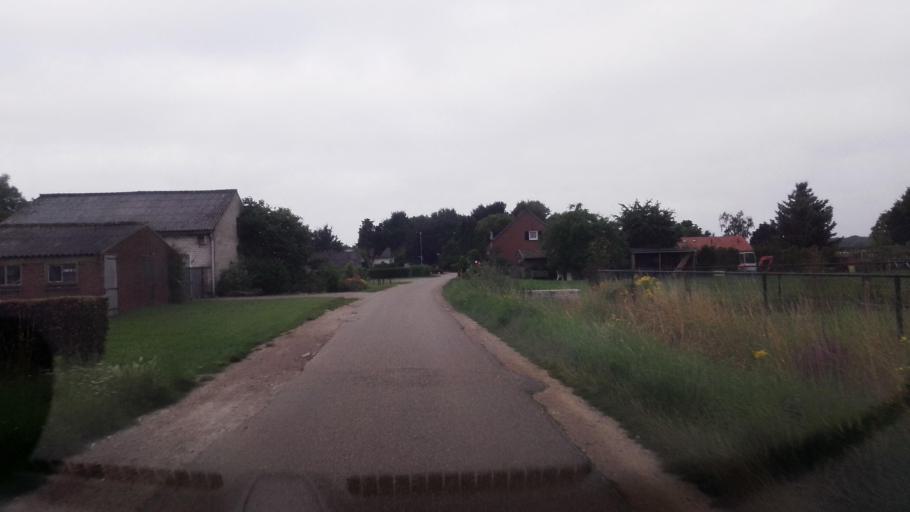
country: NL
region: Limburg
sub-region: Gemeente Venlo
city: Venlo
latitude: 51.4142
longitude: 6.1591
